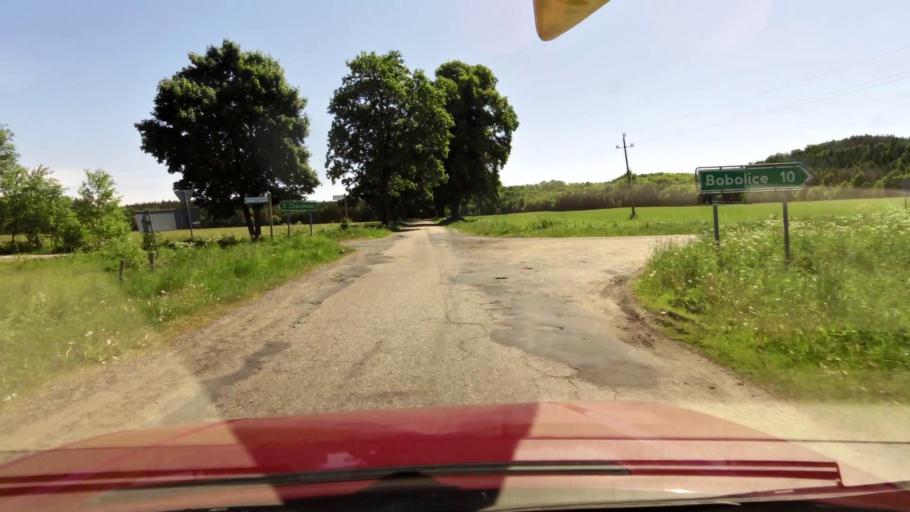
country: PL
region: West Pomeranian Voivodeship
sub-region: Powiat koszalinski
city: Bobolice
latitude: 54.0360
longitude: 16.6090
